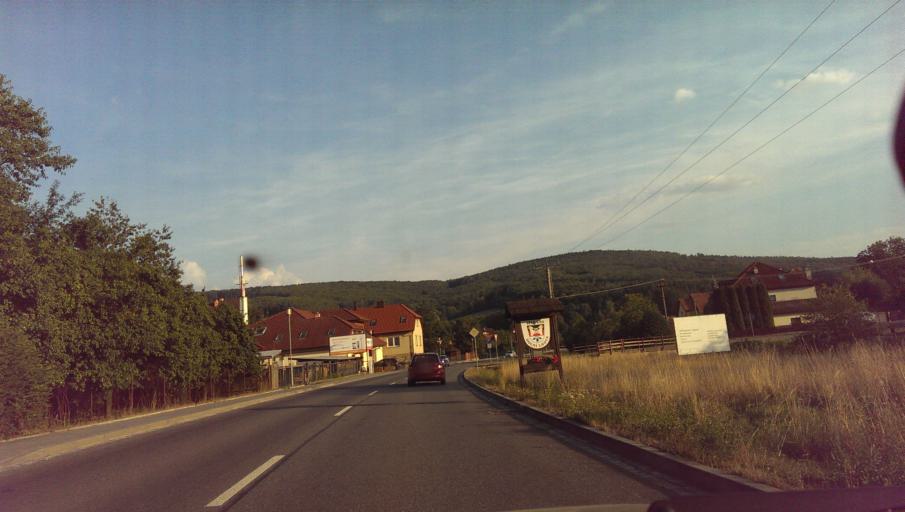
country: CZ
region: Zlin
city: Pozlovice
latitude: 49.1408
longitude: 17.8113
